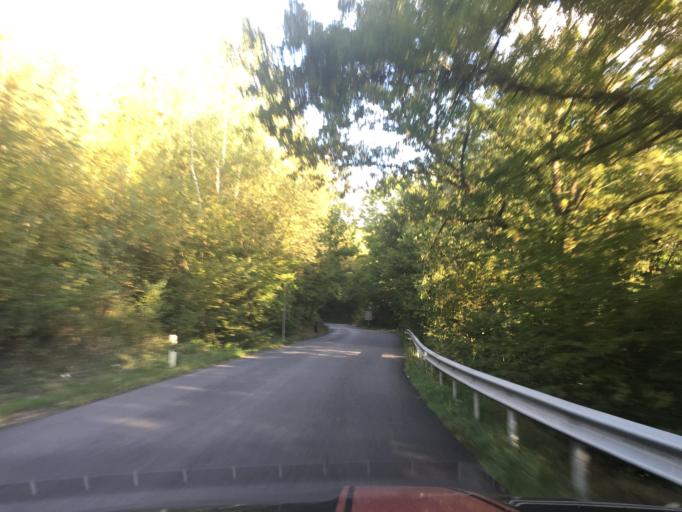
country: FR
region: Lorraine
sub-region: Departement de Meurthe-et-Moselle
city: Hussigny-Godbrange
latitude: 49.4996
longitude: 5.8689
